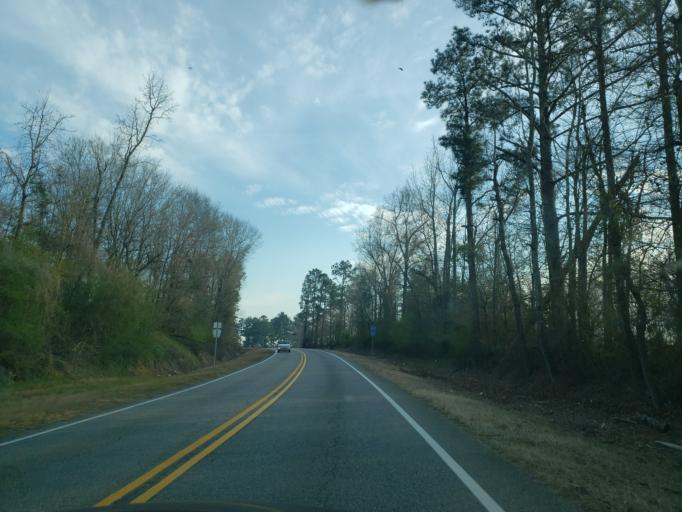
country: US
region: Alabama
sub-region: Hale County
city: Moundville
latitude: 32.9679
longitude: -87.6252
